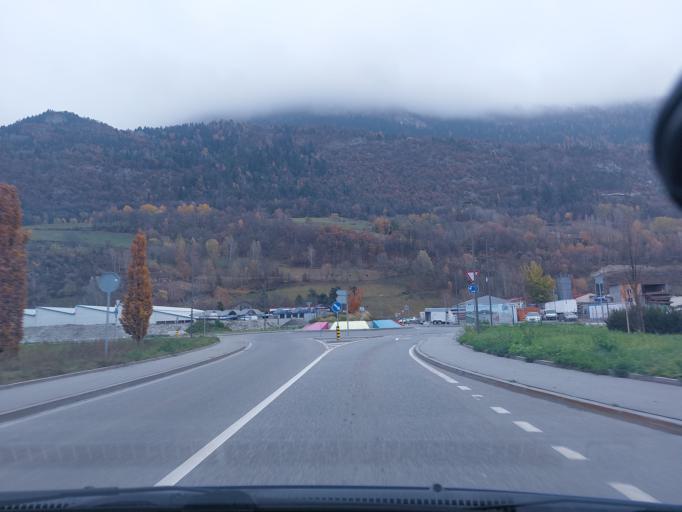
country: CH
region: Valais
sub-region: Sierre District
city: Chalais
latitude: 46.2732
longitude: 7.5187
